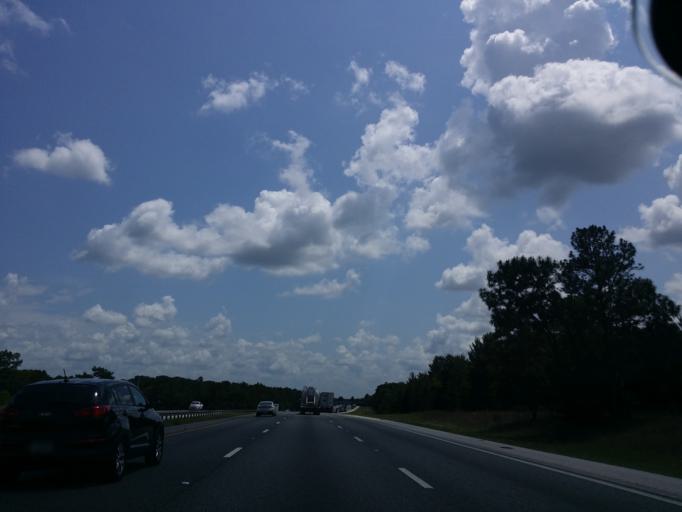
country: US
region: Florida
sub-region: Marion County
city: Belleview
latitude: 29.0601
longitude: -82.1734
